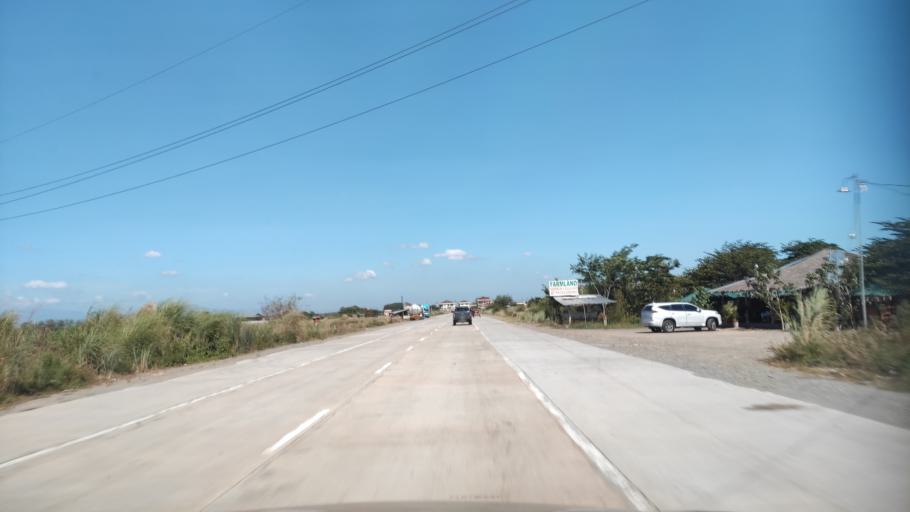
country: PH
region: Central Luzon
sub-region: Province of Tarlac
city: Salcedo
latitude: 15.8702
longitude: 120.6094
